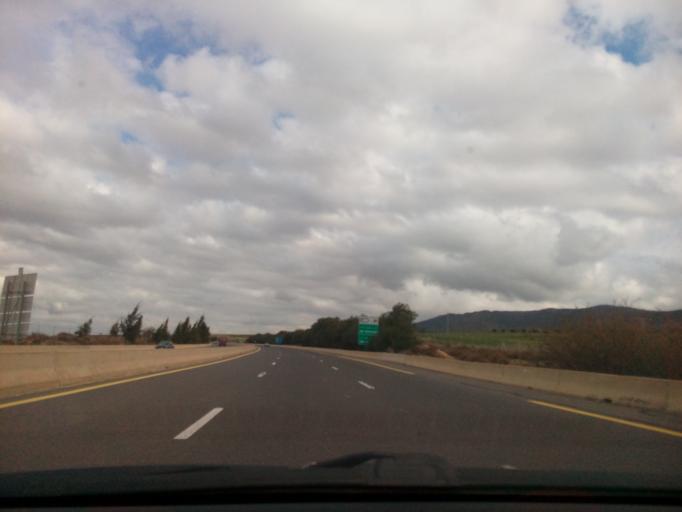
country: DZ
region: Tlemcen
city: Bensekrane
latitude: 34.9930
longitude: -1.2007
